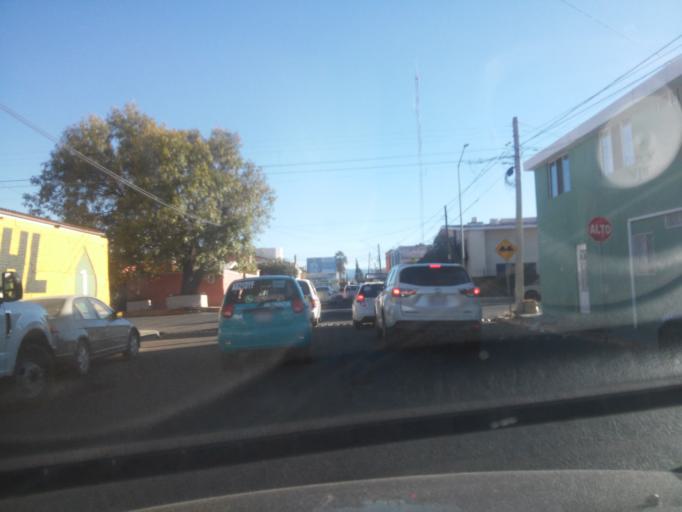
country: MX
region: Durango
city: Victoria de Durango
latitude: 24.0282
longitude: -104.6471
